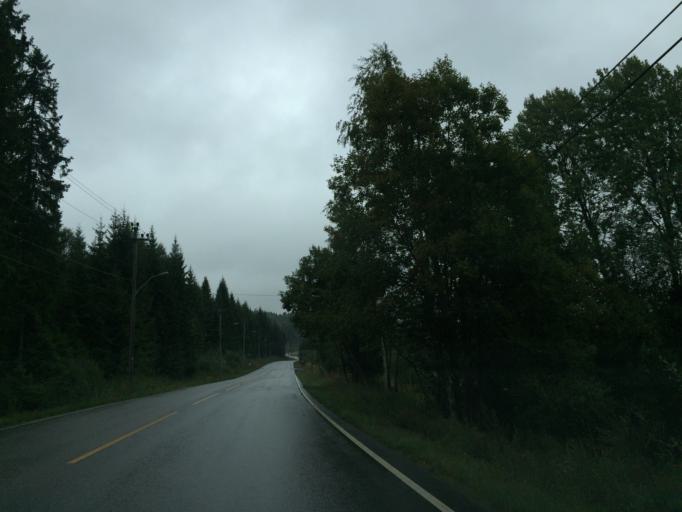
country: NO
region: Akershus
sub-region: Baerum
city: Lysaker
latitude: 59.9980
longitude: 10.6200
